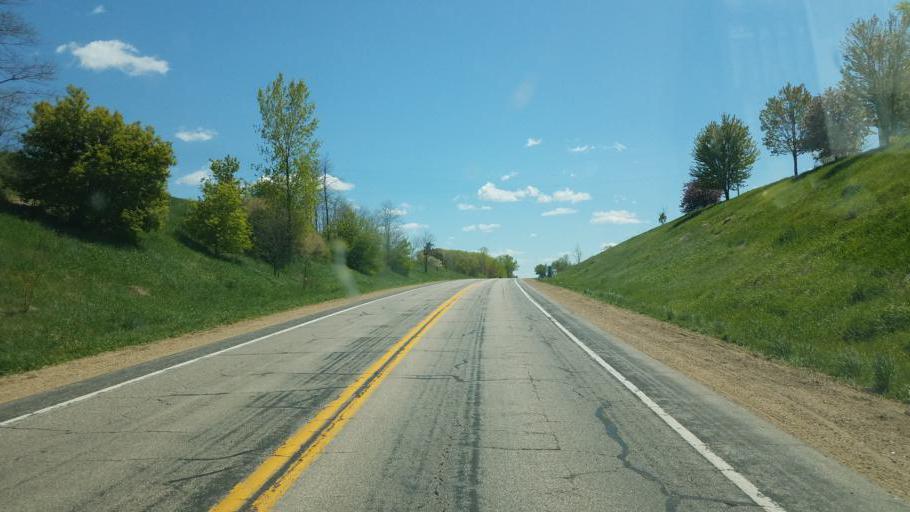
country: US
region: Wisconsin
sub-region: Vernon County
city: Hillsboro
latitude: 43.5958
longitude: -90.3522
